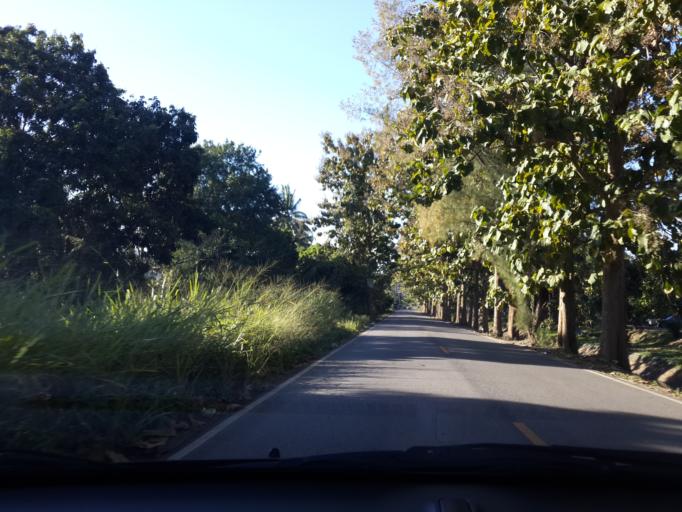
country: TH
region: Chiang Mai
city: San Sai
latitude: 18.9075
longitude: 99.1334
